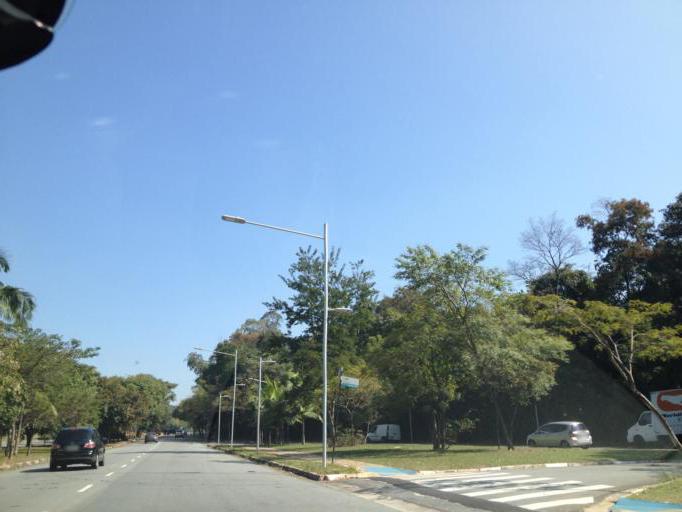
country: BR
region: Sao Paulo
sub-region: Osasco
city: Osasco
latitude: -23.5669
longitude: -46.7277
